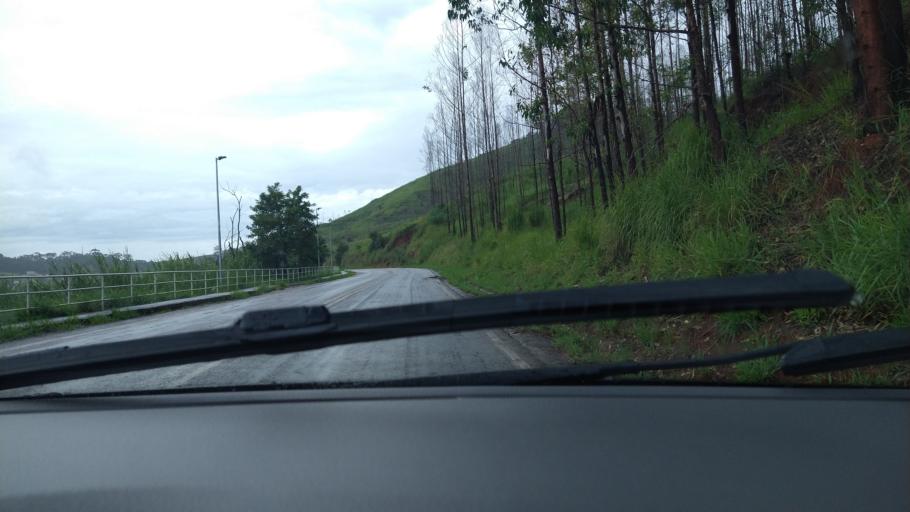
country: BR
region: Minas Gerais
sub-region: Ponte Nova
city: Ponte Nova
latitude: -20.3907
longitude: -42.9012
